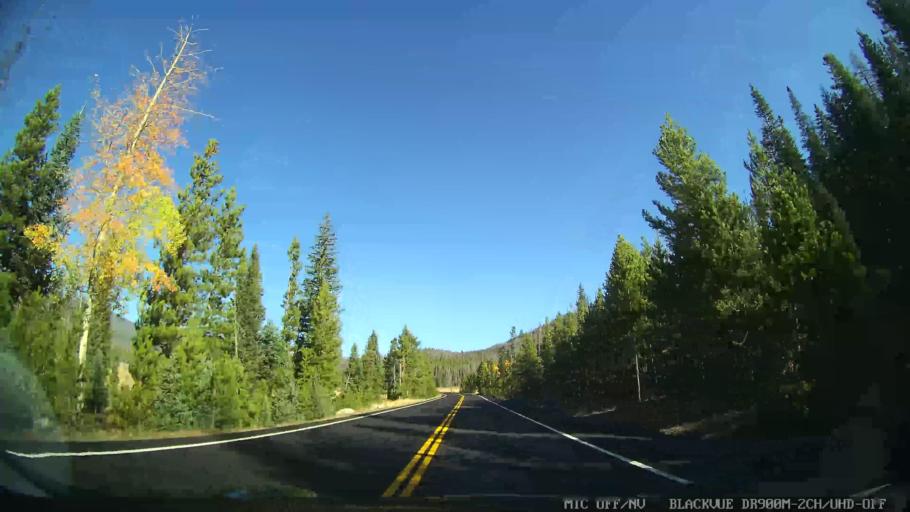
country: US
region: Colorado
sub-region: Grand County
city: Granby
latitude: 40.2782
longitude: -105.8363
